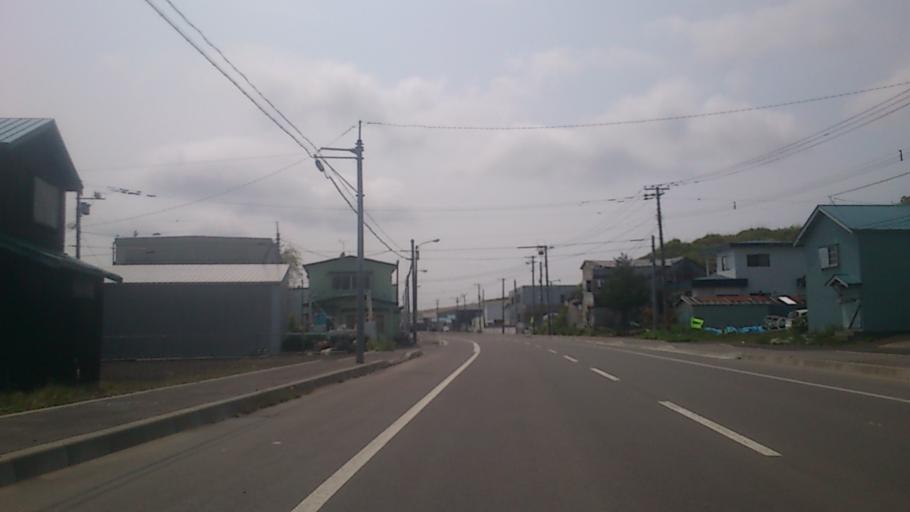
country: JP
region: Hokkaido
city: Nemuro
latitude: 43.2868
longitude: 145.5797
